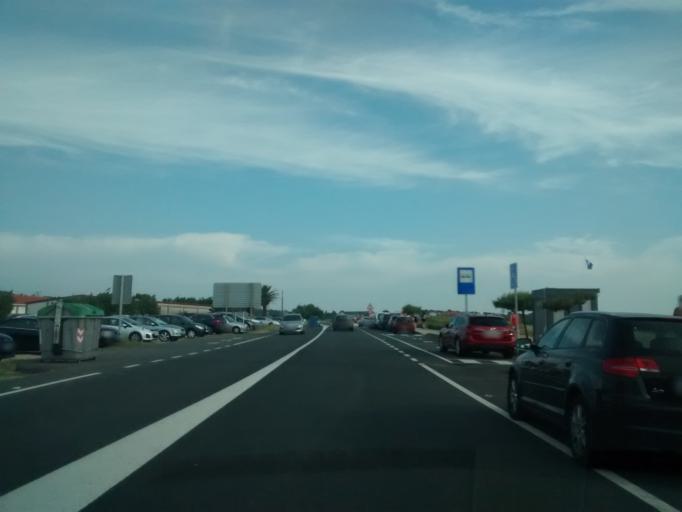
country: ES
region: Galicia
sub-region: Provincia de Pontevedra
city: O Grove
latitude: 42.4389
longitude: -8.8712
